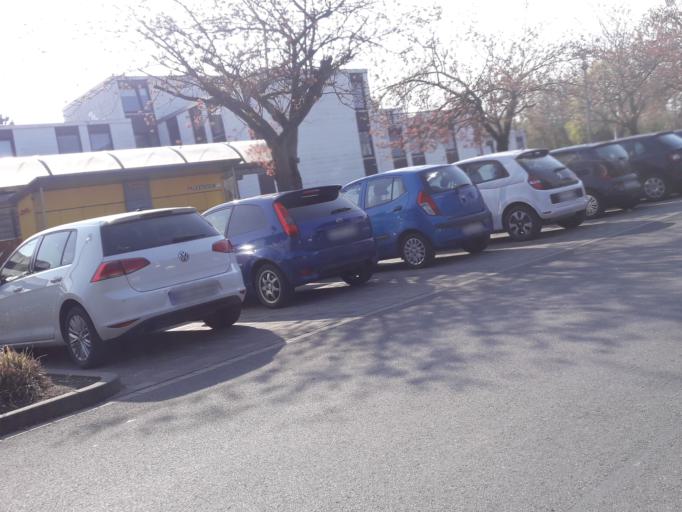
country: DE
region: North Rhine-Westphalia
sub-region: Regierungsbezirk Detmold
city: Paderborn
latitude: 51.7300
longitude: 8.7382
